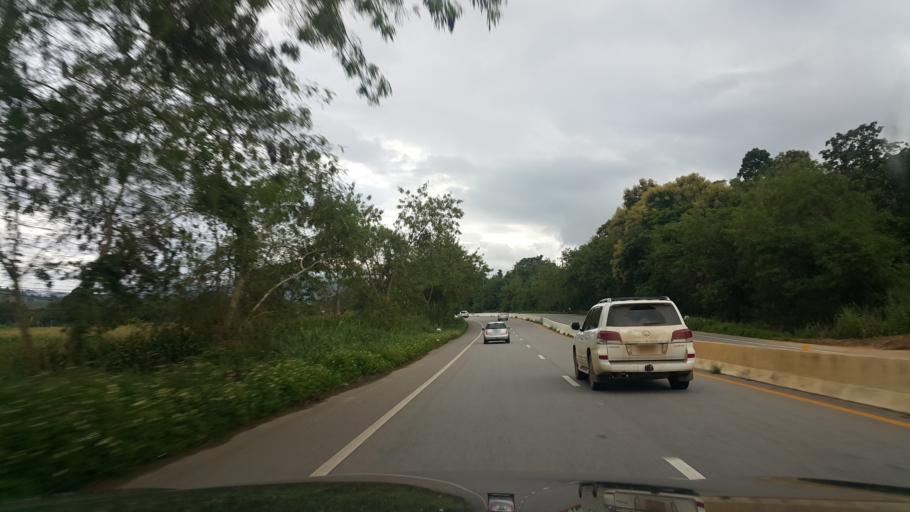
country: TH
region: Lampang
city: Wang Nuea
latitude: 19.1592
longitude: 99.5020
